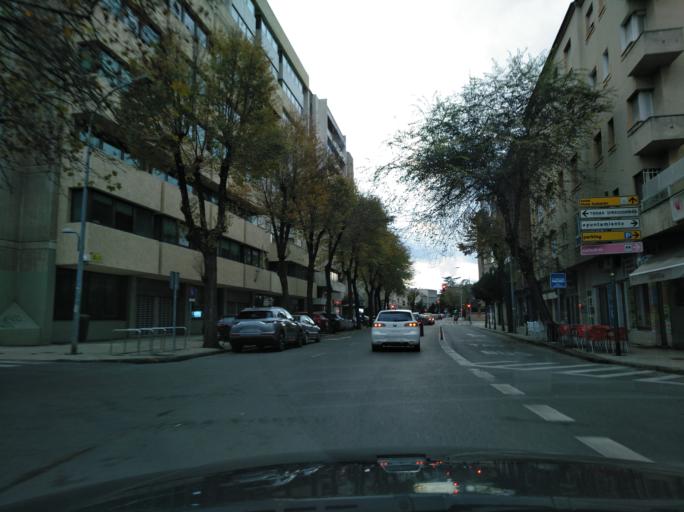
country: ES
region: Extremadura
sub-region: Provincia de Badajoz
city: Badajoz
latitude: 38.8753
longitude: -6.9712
